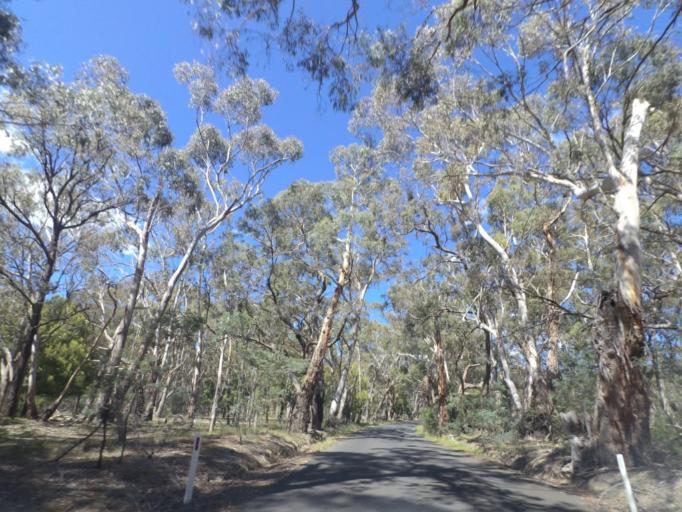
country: AU
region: Victoria
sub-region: Hume
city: Sunbury
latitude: -37.4197
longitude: 144.6275
